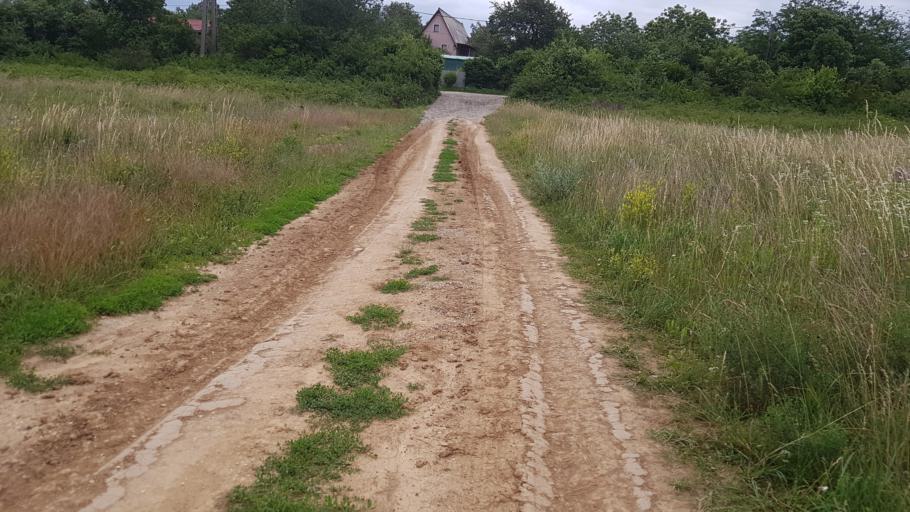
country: HU
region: Pest
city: Urom
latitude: 47.6090
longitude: 19.0282
